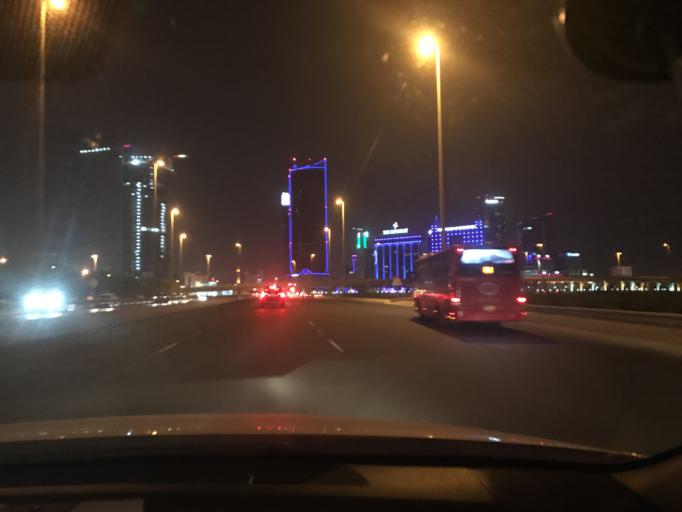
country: BH
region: Muharraq
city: Al Muharraq
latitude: 26.2443
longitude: 50.5978
